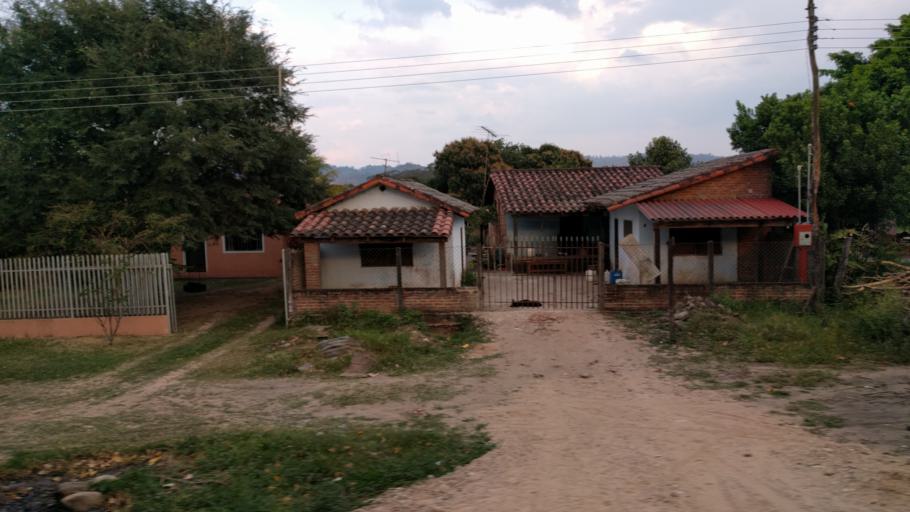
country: BO
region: Santa Cruz
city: Jorochito
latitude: -18.1286
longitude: -63.4679
